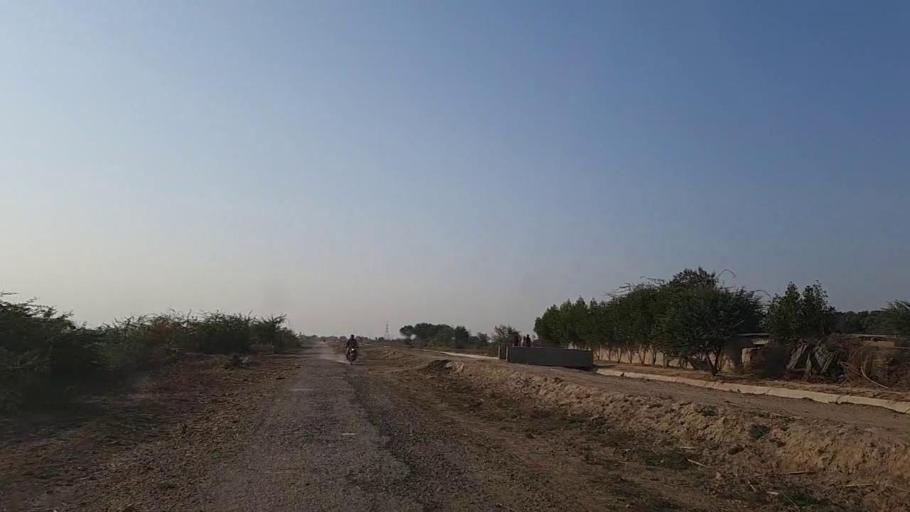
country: PK
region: Sindh
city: Naukot
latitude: 24.9154
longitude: 69.4480
